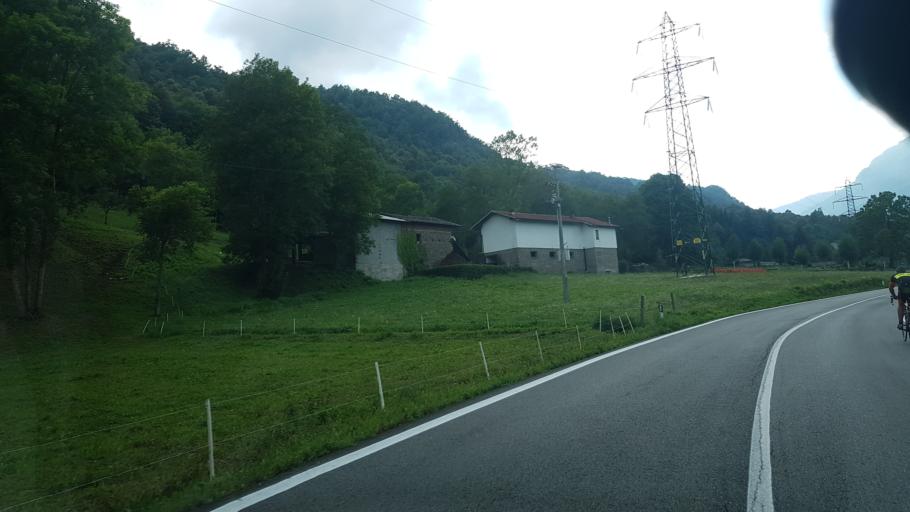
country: IT
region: Piedmont
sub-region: Provincia di Cuneo
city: Melle
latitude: 44.5618
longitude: 7.3091
